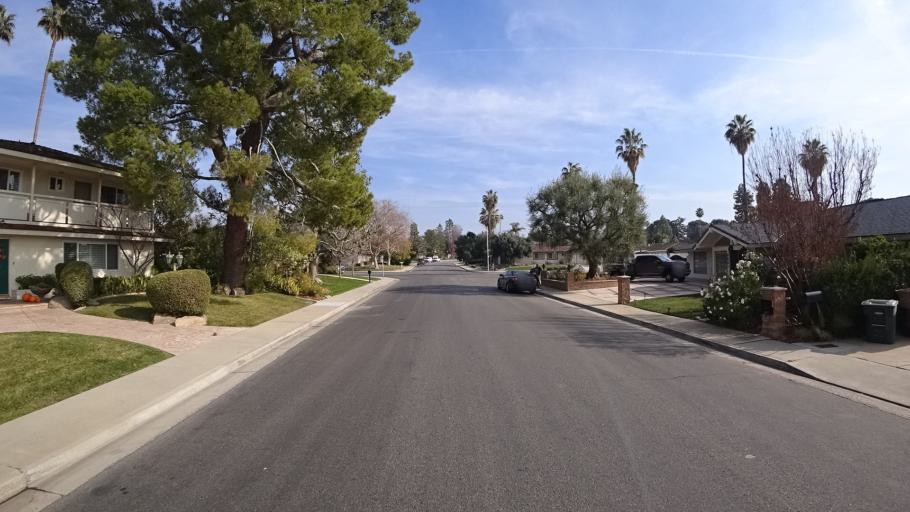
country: US
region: California
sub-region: Kern County
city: Oildale
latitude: 35.4129
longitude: -118.9637
